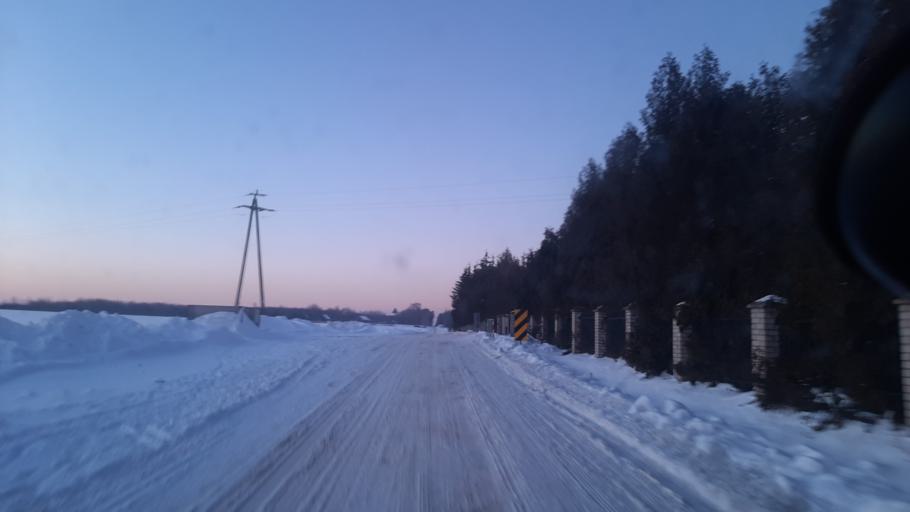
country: PL
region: Lublin Voivodeship
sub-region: Powiat lubelski
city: Jastkow
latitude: 51.3653
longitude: 22.5274
